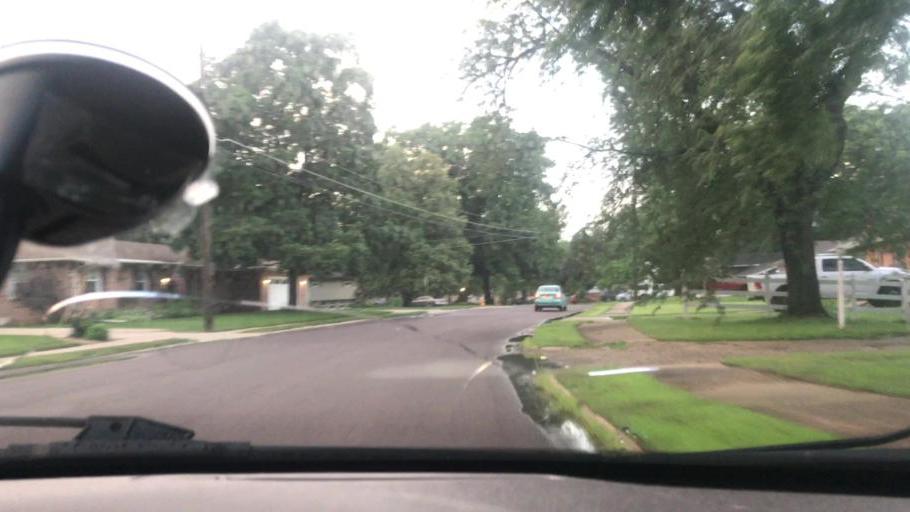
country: US
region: Illinois
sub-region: Tazewell County
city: Pekin
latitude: 40.5469
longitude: -89.6139
